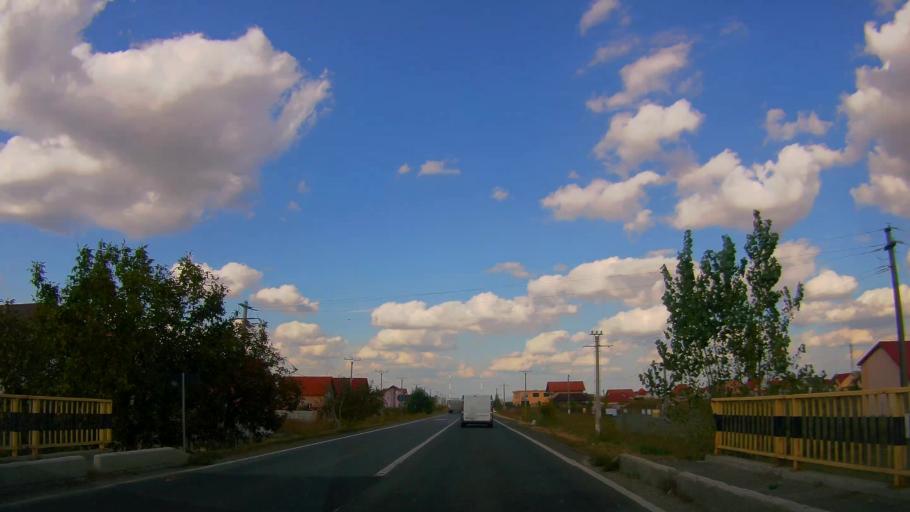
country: RO
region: Satu Mare
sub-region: Comuna Botiz
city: Botiz
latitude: 47.8368
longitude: 22.9583
